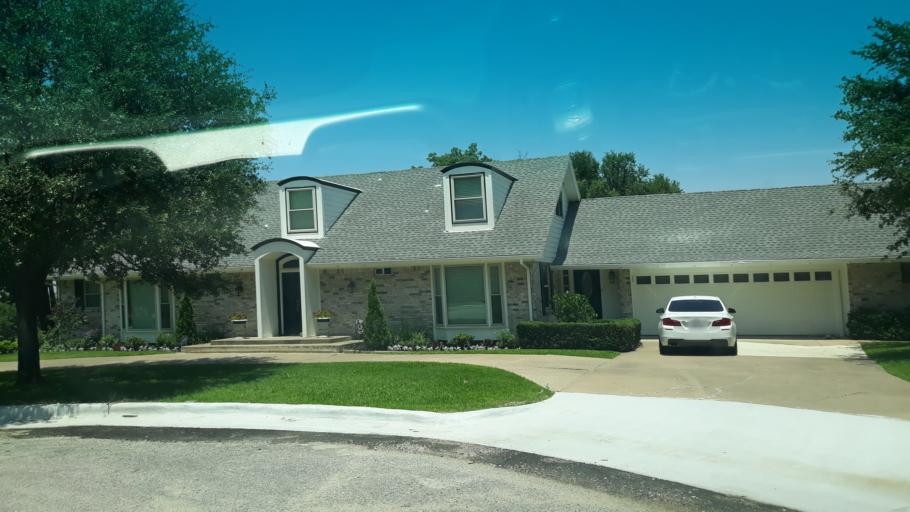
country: US
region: Texas
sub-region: Dallas County
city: Irving
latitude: 32.8585
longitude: -96.9557
